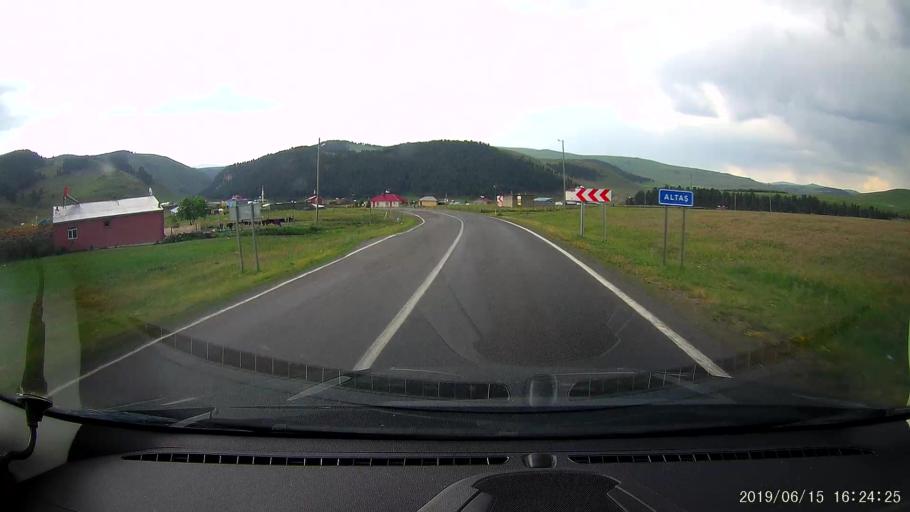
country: TR
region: Ardahan
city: Hanak
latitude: 41.1651
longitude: 42.8702
